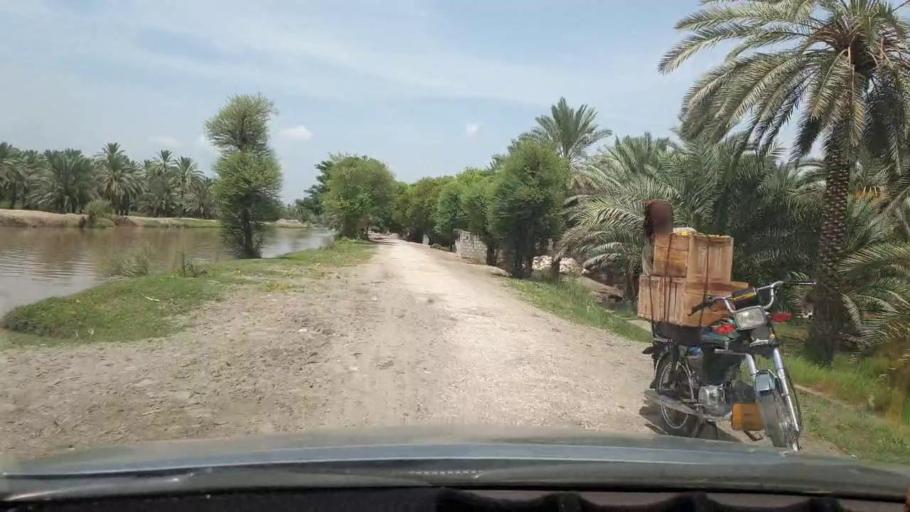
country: PK
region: Sindh
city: Khairpur
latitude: 27.4506
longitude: 68.7979
